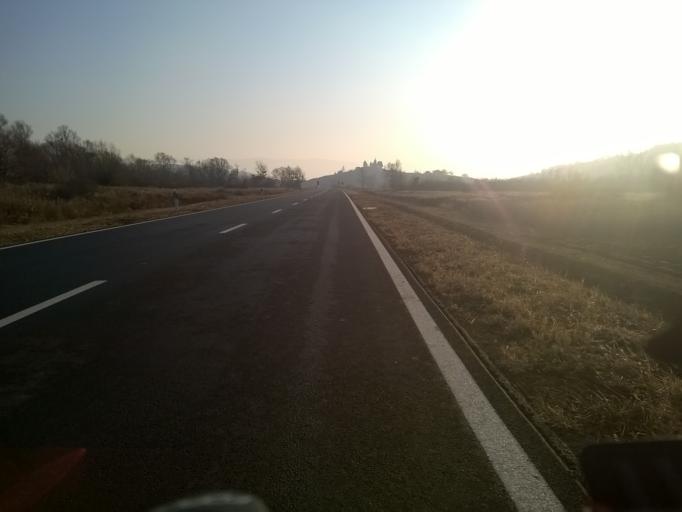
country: HR
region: Krapinsko-Zagorska
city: Zabok
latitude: 46.0493
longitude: 15.9134
